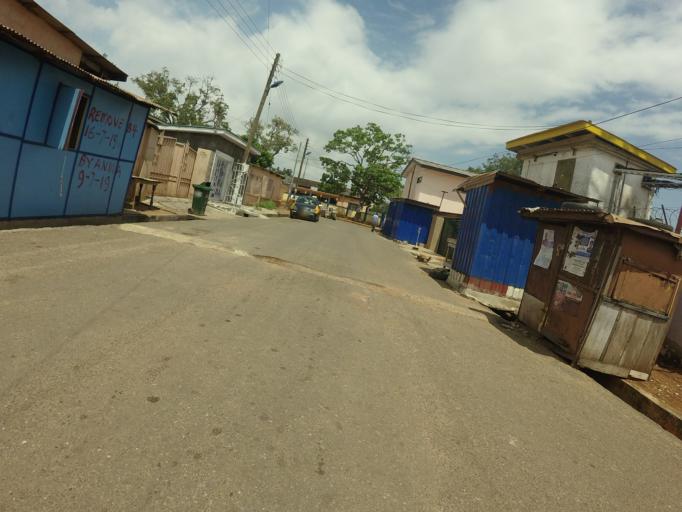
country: GH
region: Greater Accra
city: Accra
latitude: 5.5910
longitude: -0.2044
